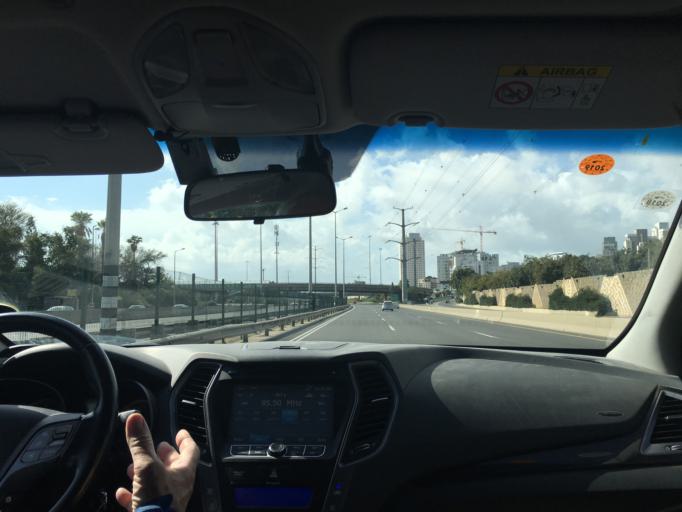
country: IL
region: Tel Aviv
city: Giv`at Shemu'el
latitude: 32.0677
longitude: 34.8400
